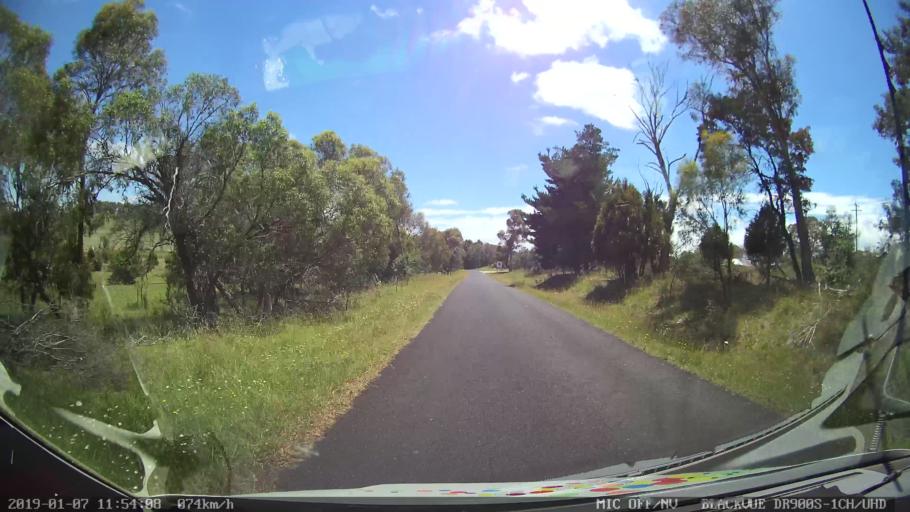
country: AU
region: New South Wales
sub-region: Guyra
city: Guyra
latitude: -30.2994
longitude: 151.6639
